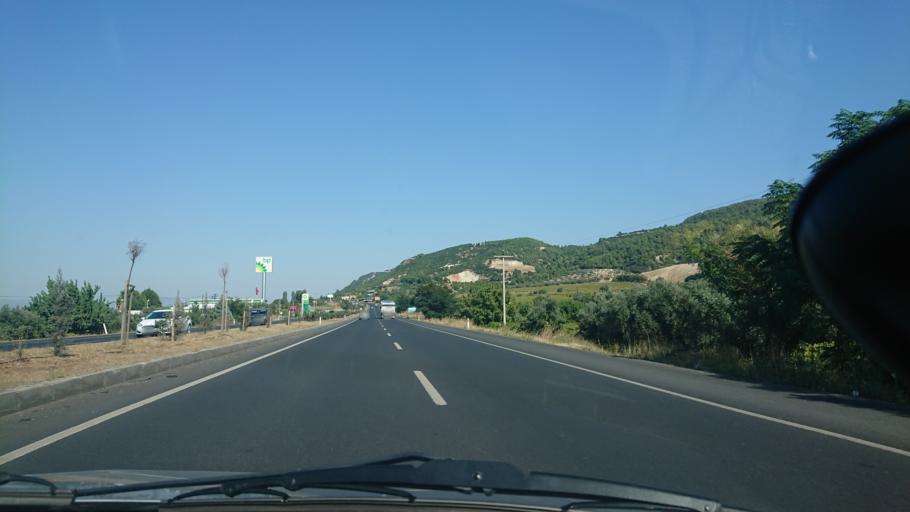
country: TR
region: Manisa
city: Turgutlu
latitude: 38.4836
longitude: 27.8206
